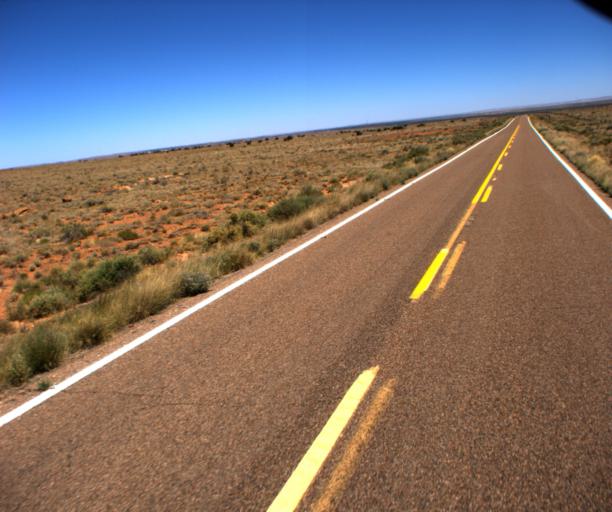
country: US
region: Arizona
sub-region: Navajo County
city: Winslow
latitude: 34.9218
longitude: -110.6378
